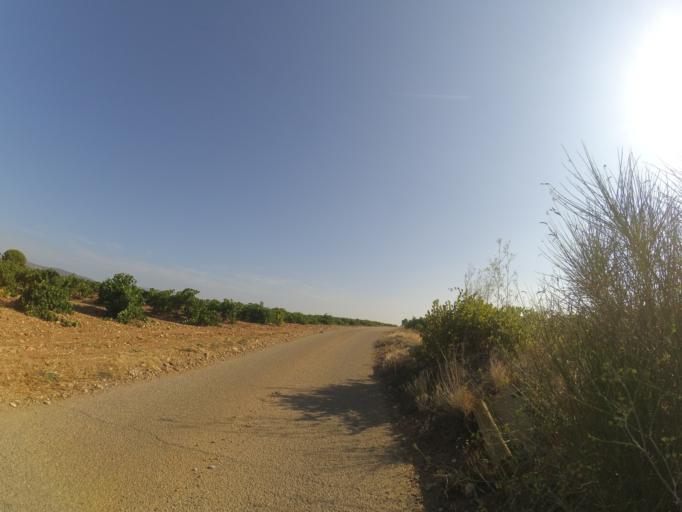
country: FR
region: Languedoc-Roussillon
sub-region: Departement des Pyrenees-Orientales
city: Rivesaltes
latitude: 42.7921
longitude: 2.8478
